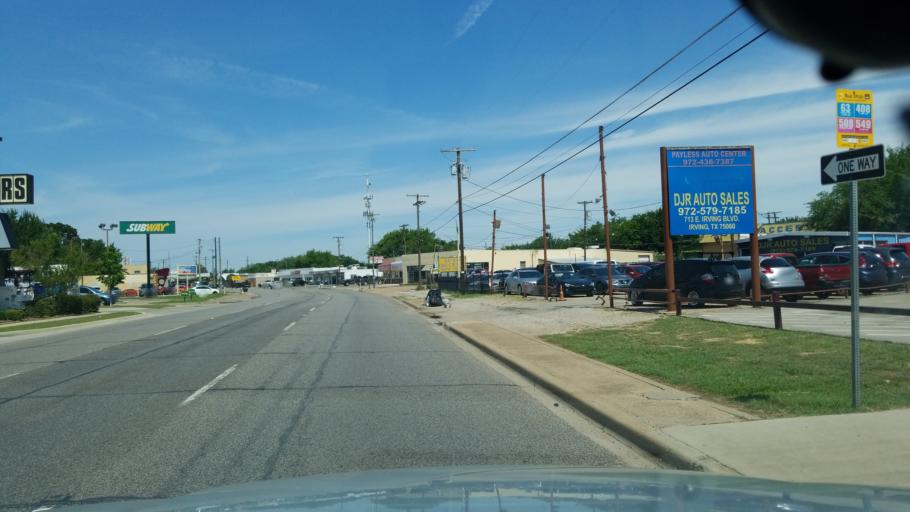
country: US
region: Texas
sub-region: Dallas County
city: Irving
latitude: 32.8132
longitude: -96.9376
